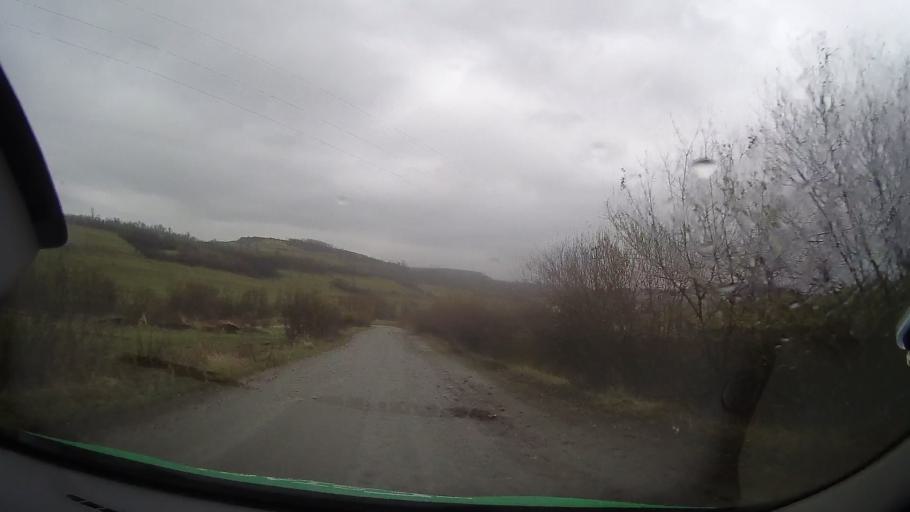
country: RO
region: Bistrita-Nasaud
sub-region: Comuna Monor
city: Monor
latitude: 46.9495
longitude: 24.7140
